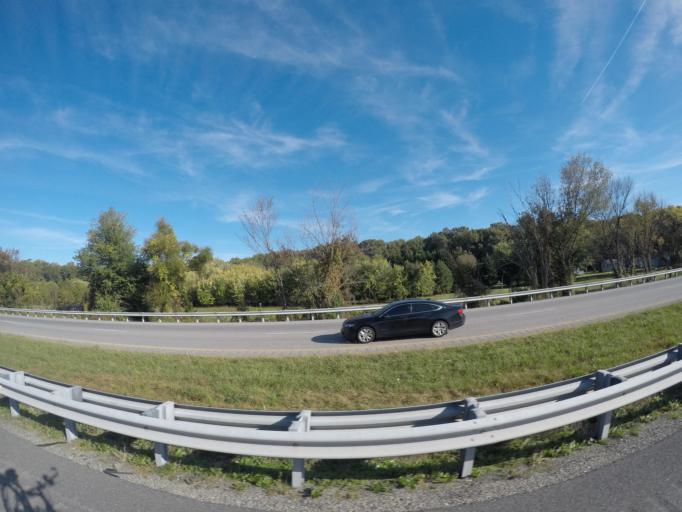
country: US
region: Maryland
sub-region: Queen Anne's County
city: Grasonville
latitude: 38.9817
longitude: -76.1445
